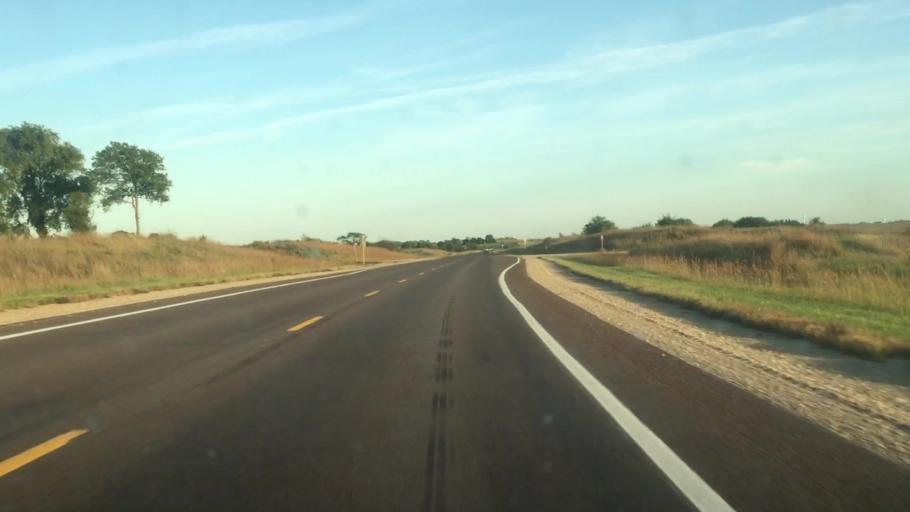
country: US
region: Kansas
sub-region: Atchison County
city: Atchison
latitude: 39.4272
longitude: -95.0736
